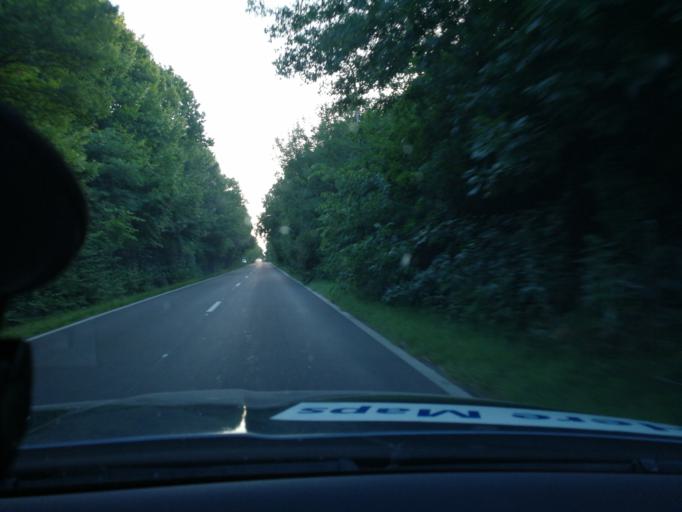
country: RO
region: Constanta
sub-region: Comuna Douazeci si Trei August
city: Douazeci si Trei August
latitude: 43.8750
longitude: 28.5905
